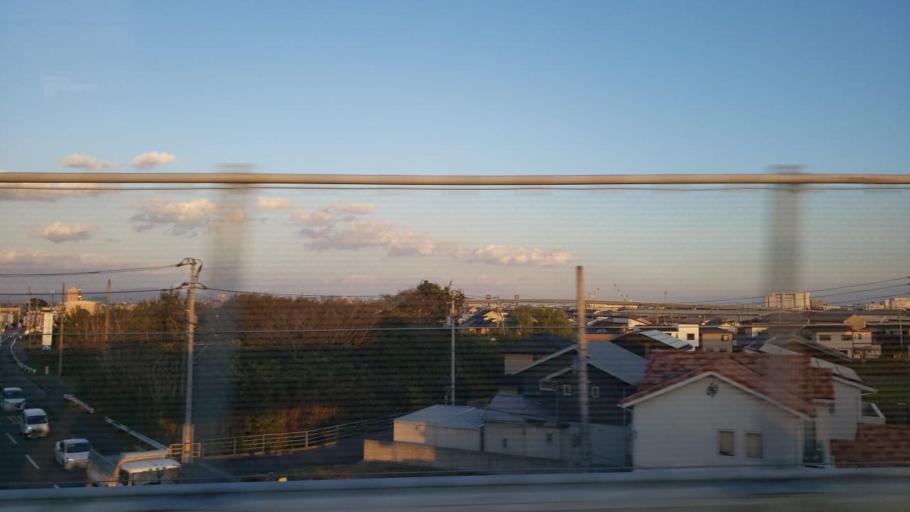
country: JP
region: Tokushima
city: Tokushima-shi
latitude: 34.1308
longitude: 134.5646
